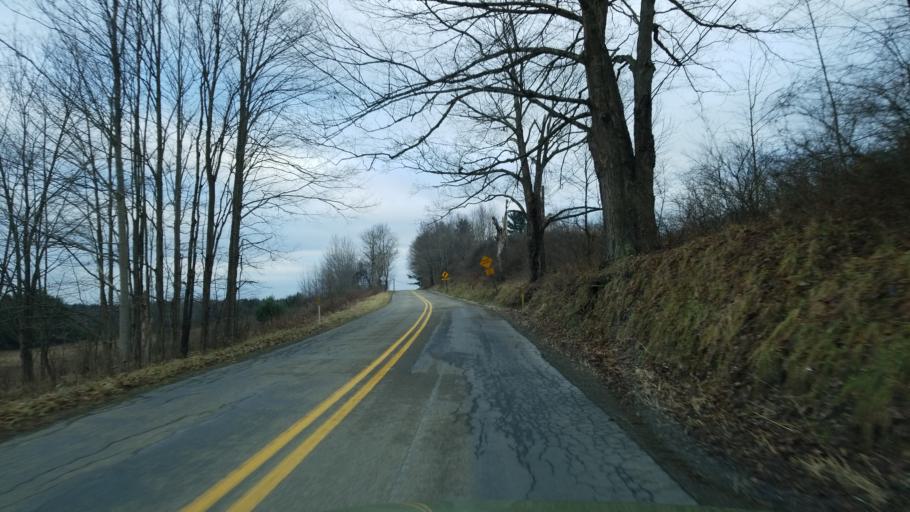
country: US
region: Pennsylvania
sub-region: Jefferson County
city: Falls Creek
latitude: 41.1781
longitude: -78.8144
